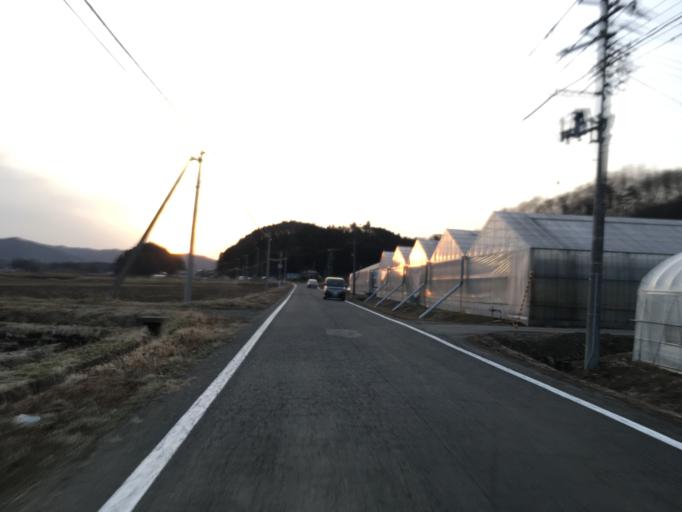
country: JP
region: Fukushima
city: Ishikawa
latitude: 37.0664
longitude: 140.3334
